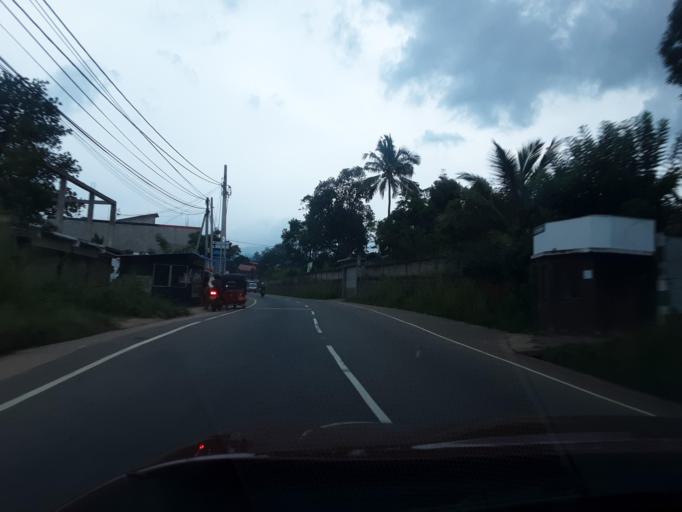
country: LK
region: Central
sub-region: Nuwara Eliya District
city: Nuwara Eliya
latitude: 6.9016
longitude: 80.8995
